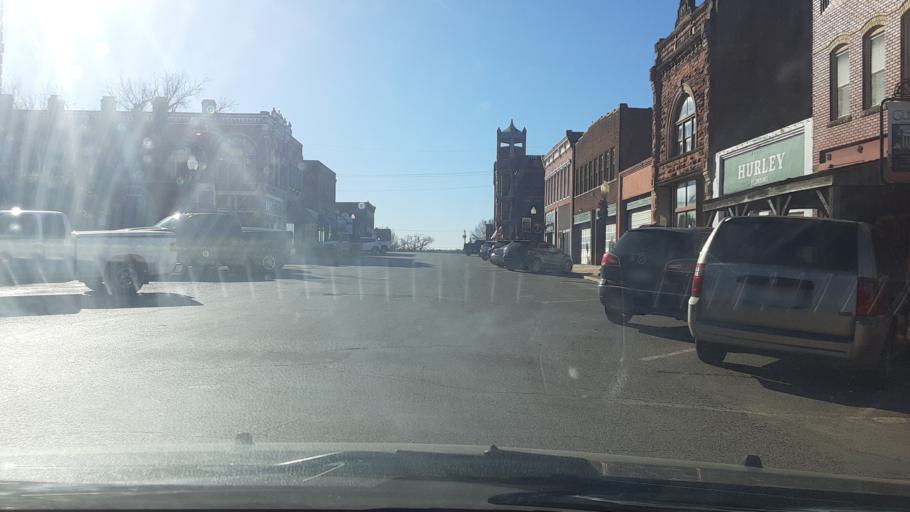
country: US
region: Oklahoma
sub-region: Logan County
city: Guthrie
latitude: 35.8780
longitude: -97.4276
